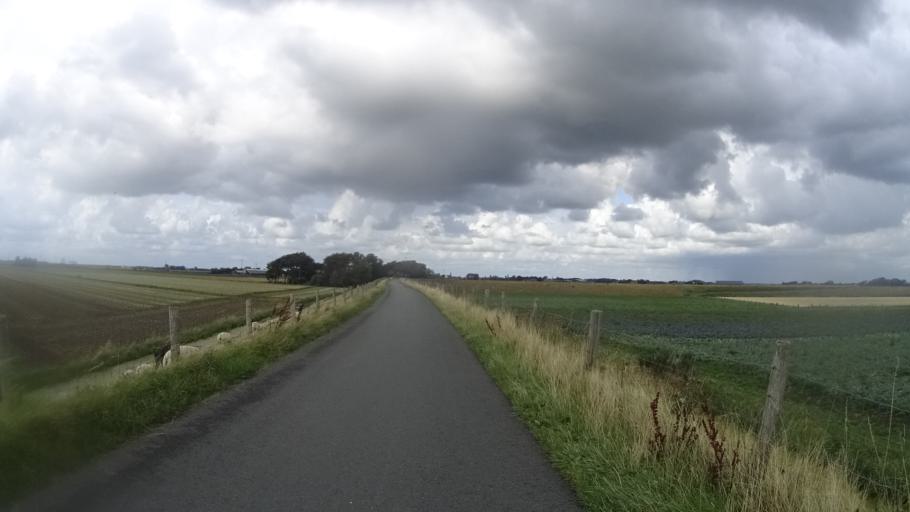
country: NL
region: North Holland
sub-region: Gemeente Schagen
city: Harenkarspel
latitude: 52.7356
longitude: 4.7061
